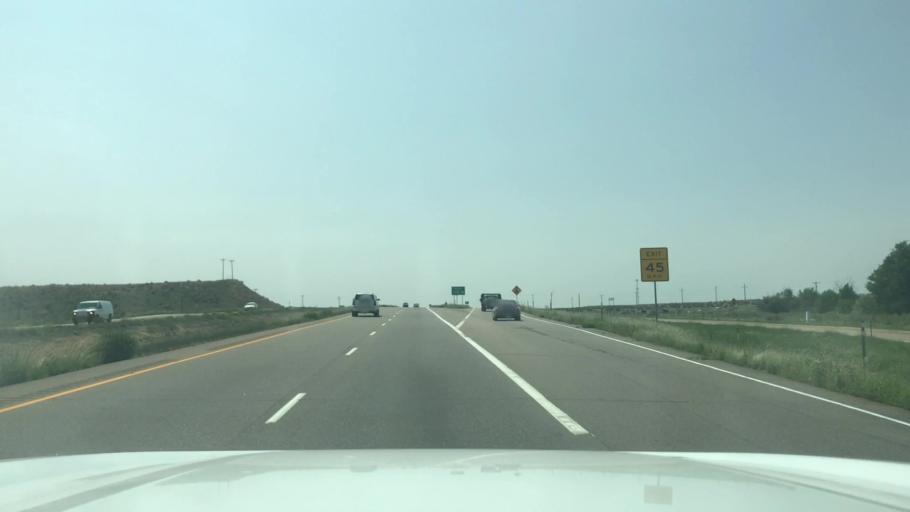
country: US
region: Colorado
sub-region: Pueblo County
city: Pueblo West
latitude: 38.4047
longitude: -104.6159
